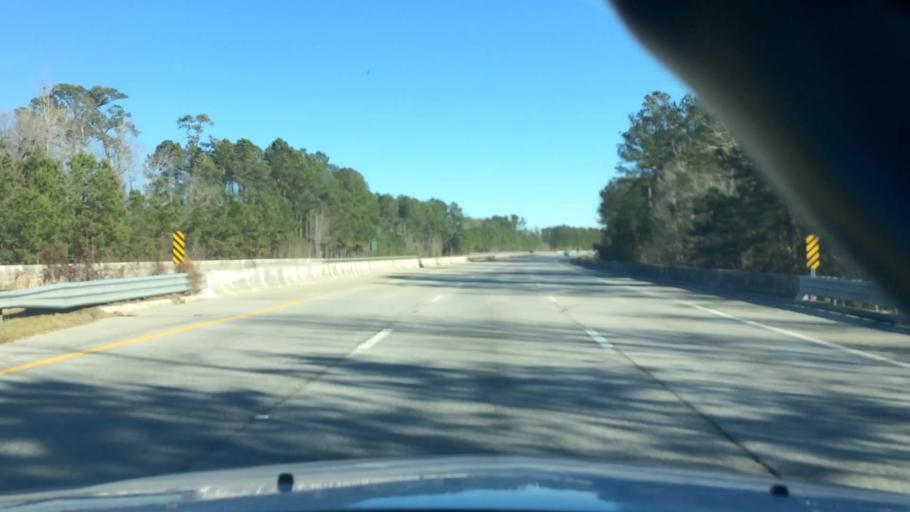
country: US
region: South Carolina
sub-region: Horry County
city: North Myrtle Beach
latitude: 33.8639
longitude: -78.6942
